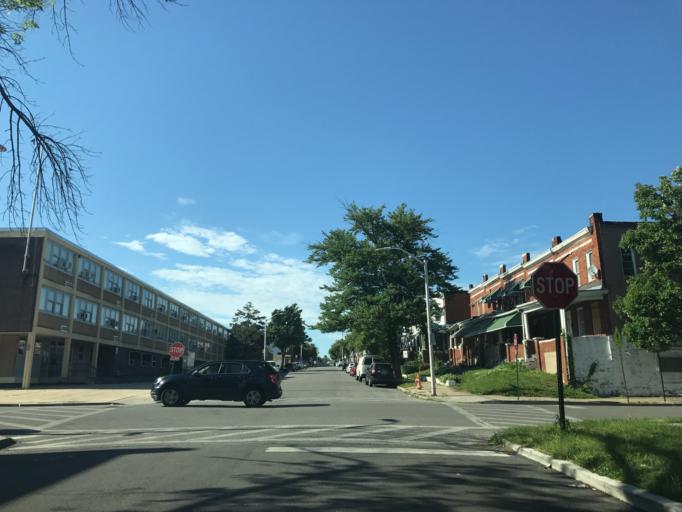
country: US
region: Maryland
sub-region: City of Baltimore
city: Baltimore
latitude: 39.3063
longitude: -76.6497
